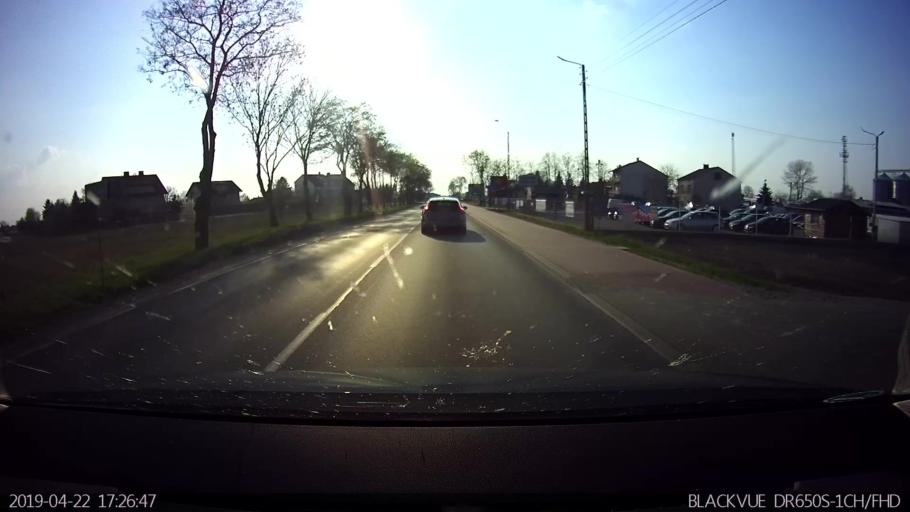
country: PL
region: Masovian Voivodeship
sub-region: Powiat sokolowski
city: Sokolow Podlaski
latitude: 52.3954
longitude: 22.2721
